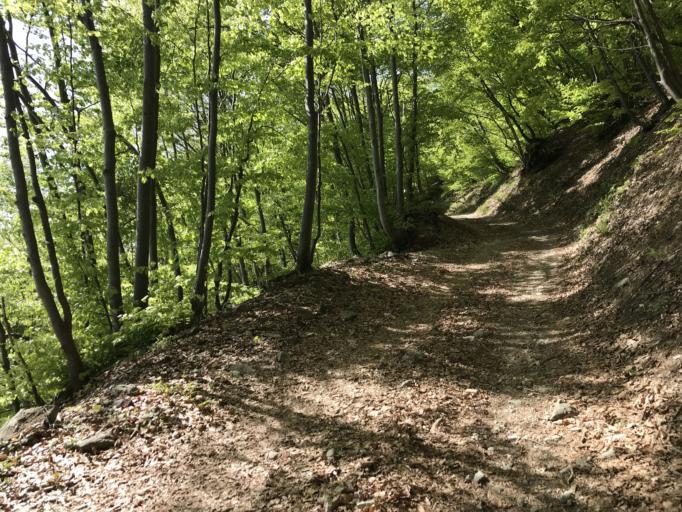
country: IT
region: Piedmont
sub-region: Provincia di Cuneo
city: Robilante
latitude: 44.2914
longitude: 7.5501
